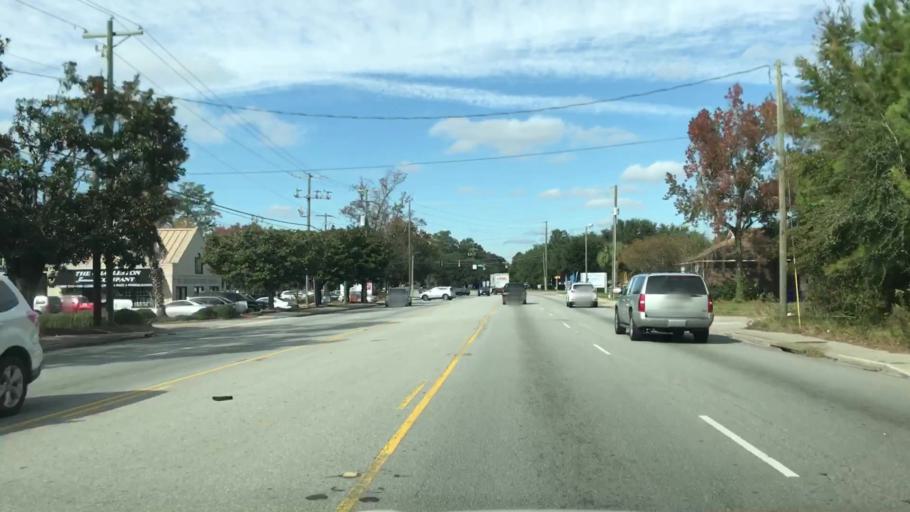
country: US
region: South Carolina
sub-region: Charleston County
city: North Charleston
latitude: 32.8059
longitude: -80.0217
